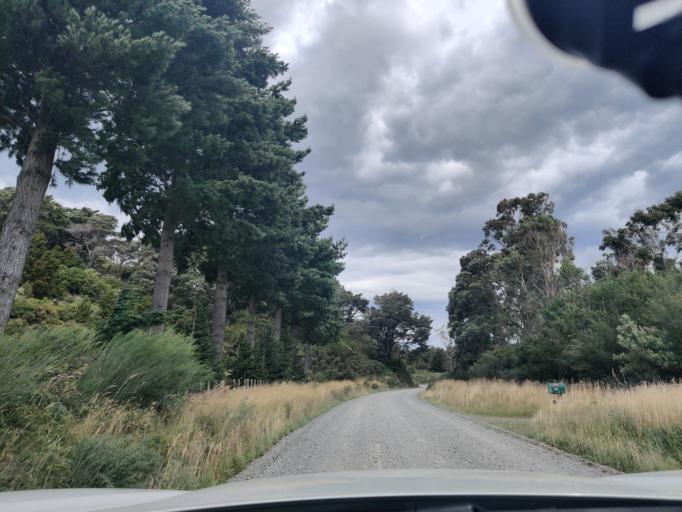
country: NZ
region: Wellington
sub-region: Masterton District
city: Masterton
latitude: -41.0386
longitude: 175.4025
